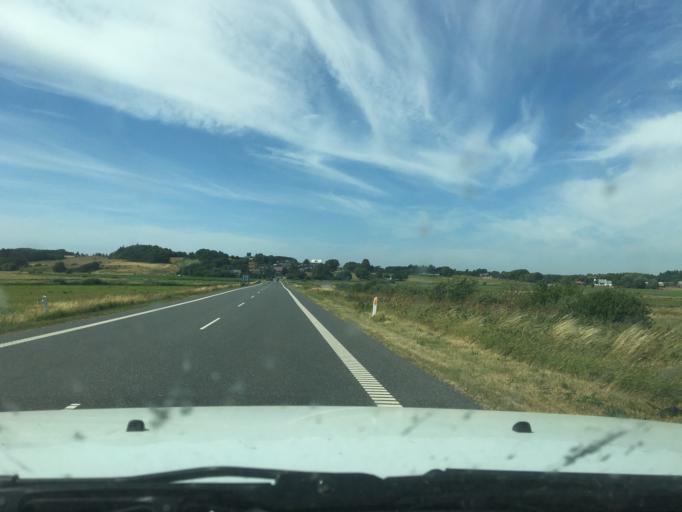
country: DK
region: Central Jutland
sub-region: Viborg Kommune
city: Viborg
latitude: 56.5700
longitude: 9.3826
